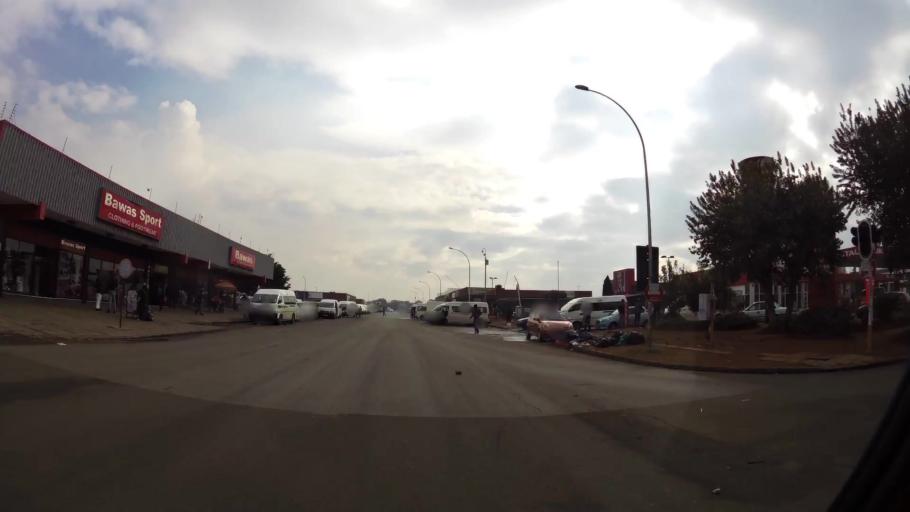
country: ZA
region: Gauteng
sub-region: Sedibeng District Municipality
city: Vanderbijlpark
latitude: -26.6976
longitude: 27.8389
